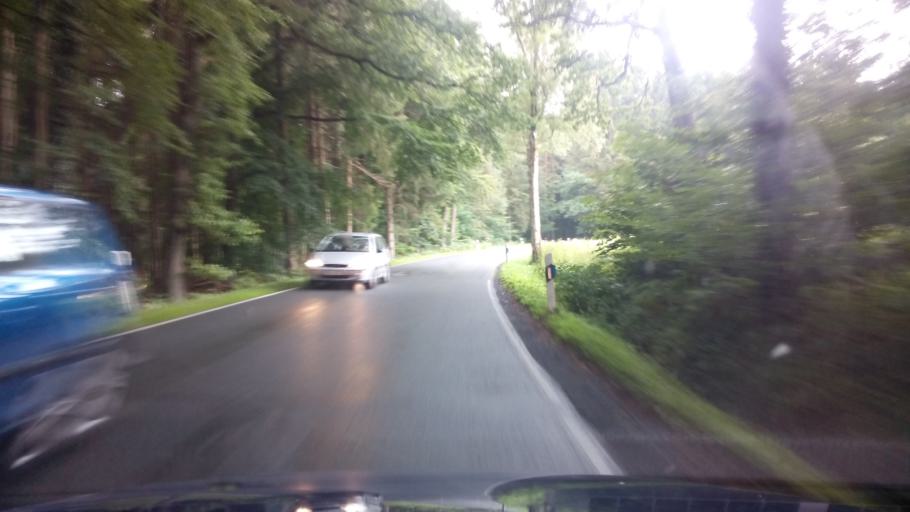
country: DE
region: Lower Saxony
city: Bad Essen
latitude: 52.2787
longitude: 8.3328
